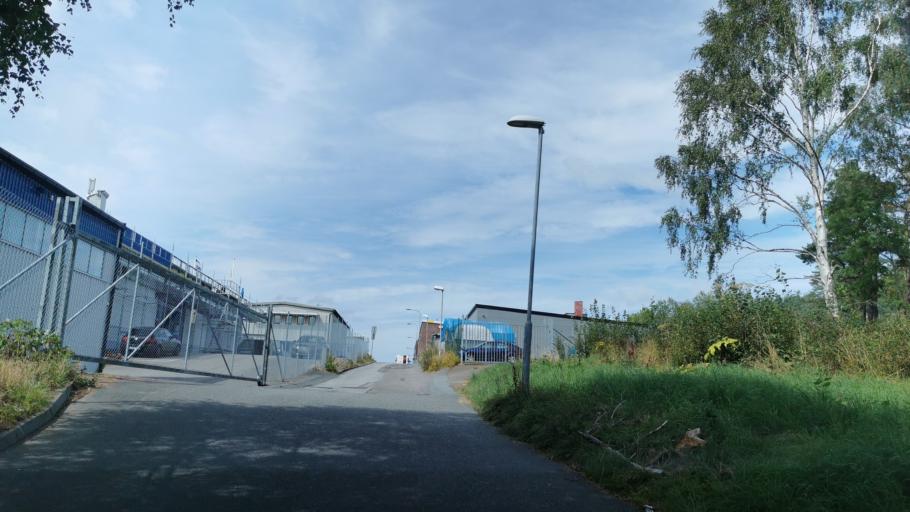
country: SE
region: Vaestra Goetaland
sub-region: Goteborg
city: Majorna
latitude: 57.6529
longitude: 11.9467
